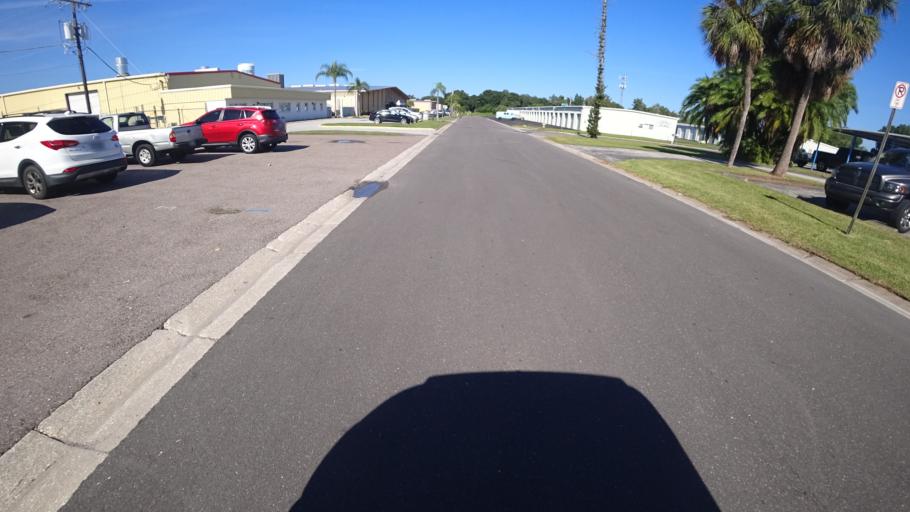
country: US
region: Florida
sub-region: Manatee County
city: Whitfield
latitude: 27.4156
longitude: -82.5392
